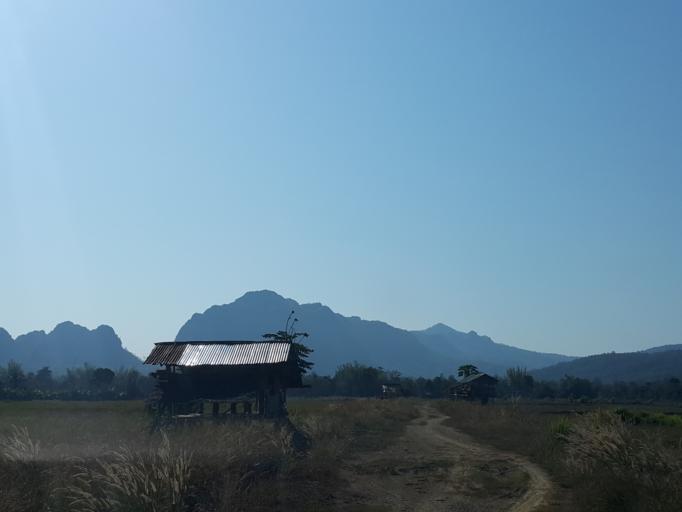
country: TH
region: Sukhothai
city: Thung Saliam
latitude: 17.3171
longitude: 99.4346
